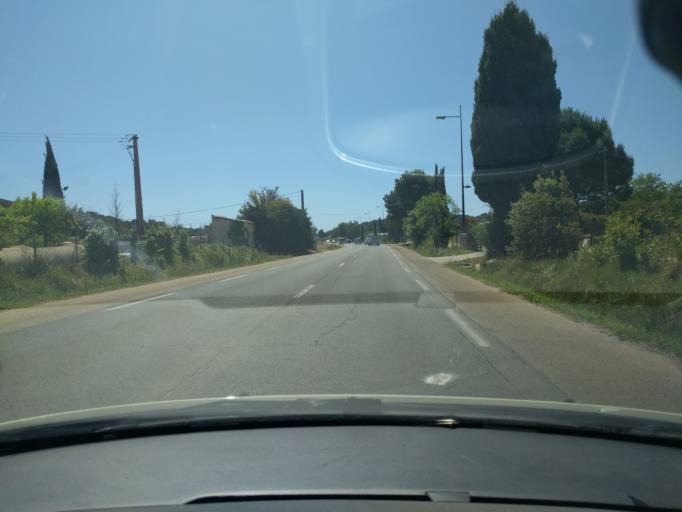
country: FR
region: Provence-Alpes-Cote d'Azur
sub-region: Departement du Var
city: Carqueiranne
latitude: 43.1064
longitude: 6.0516
